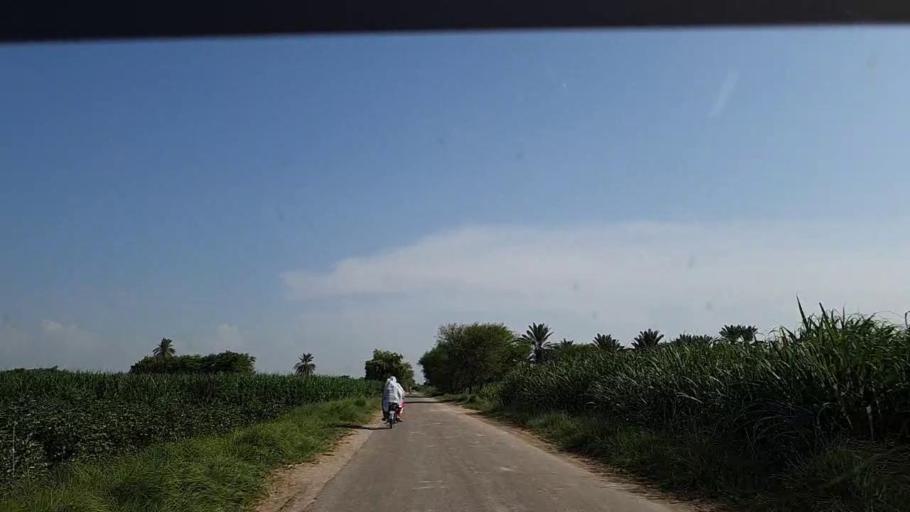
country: PK
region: Sindh
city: Adilpur
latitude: 27.9384
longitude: 69.2538
